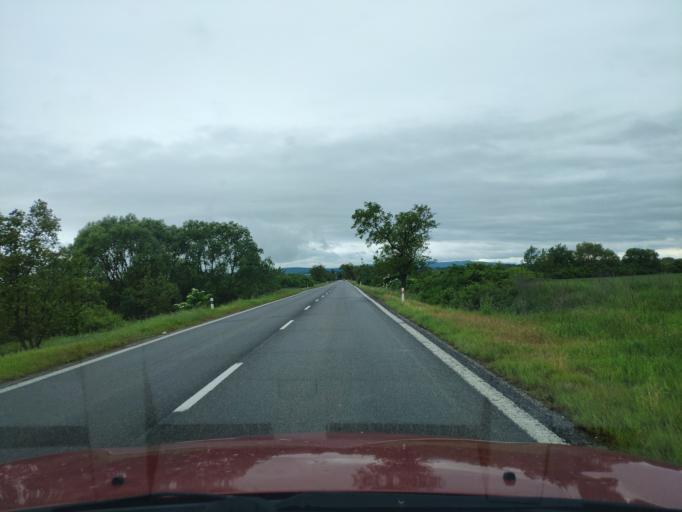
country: HU
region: Borsod-Abauj-Zemplen
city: Ricse
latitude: 48.4337
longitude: 21.8790
